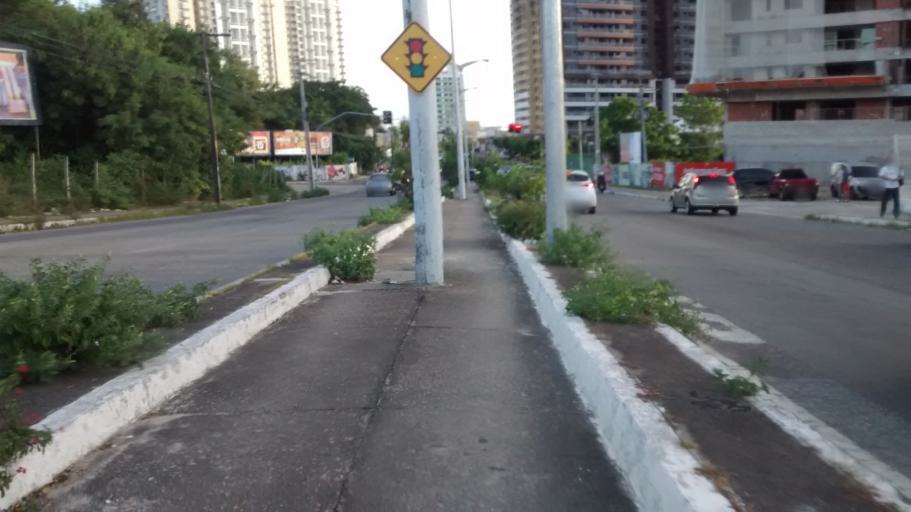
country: BR
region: Ceara
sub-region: Fortaleza
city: Fortaleza
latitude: -3.7635
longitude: -38.4945
